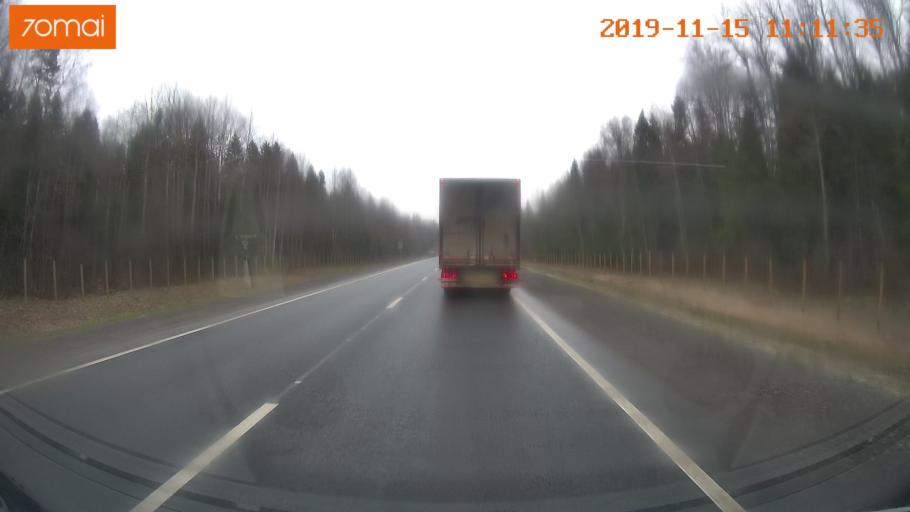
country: RU
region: Vologda
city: Chebsara
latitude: 59.1214
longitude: 39.1453
